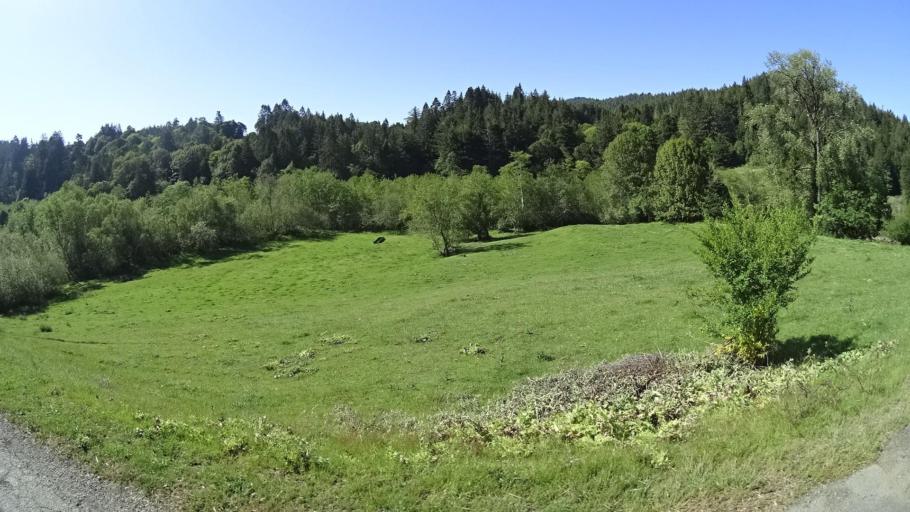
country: US
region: California
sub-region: Humboldt County
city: Fortuna
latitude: 40.5288
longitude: -124.1758
